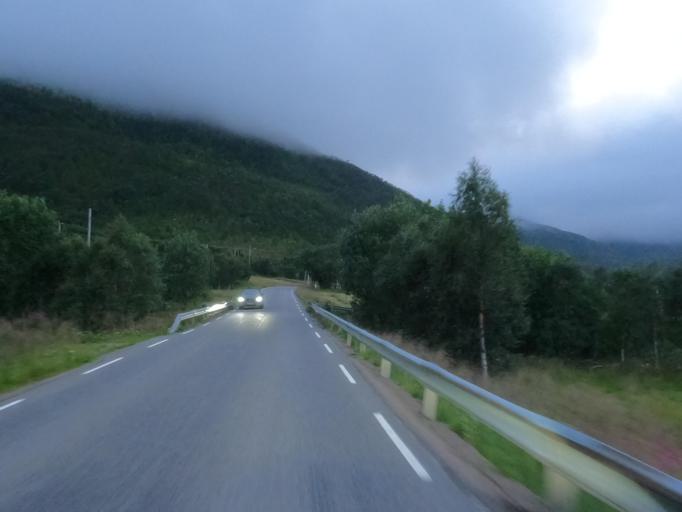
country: NO
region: Nordland
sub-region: Lodingen
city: Lodingen
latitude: 68.6037
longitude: 15.7828
